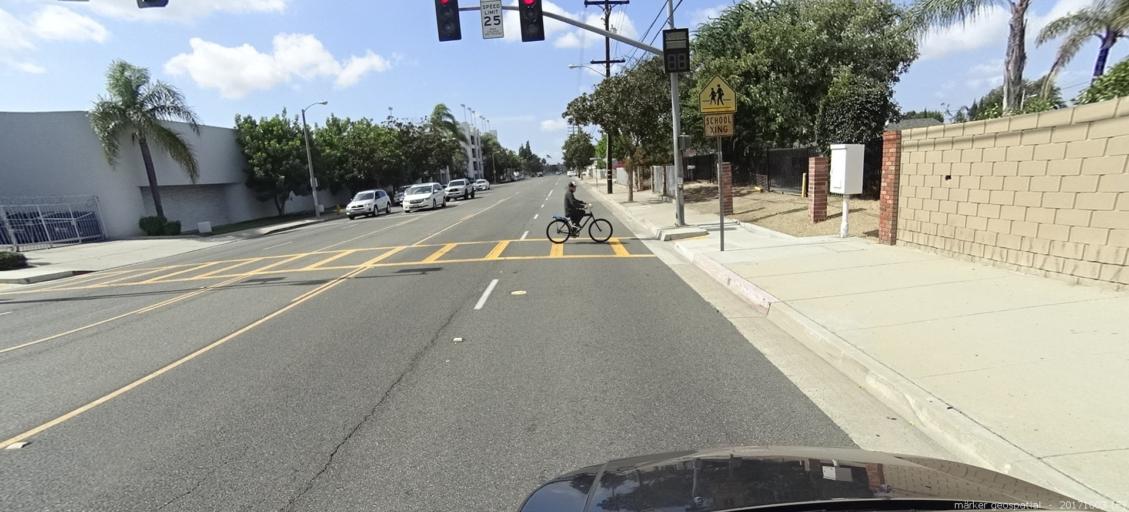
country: US
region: California
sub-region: Orange County
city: Garden Grove
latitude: 33.7668
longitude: -117.9656
